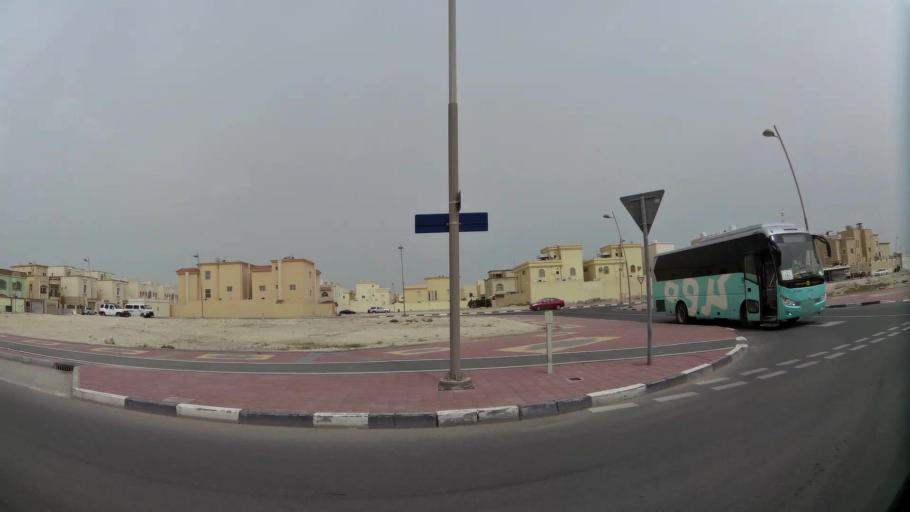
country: QA
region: Baladiyat ad Dawhah
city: Doha
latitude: 25.2312
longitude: 51.5482
